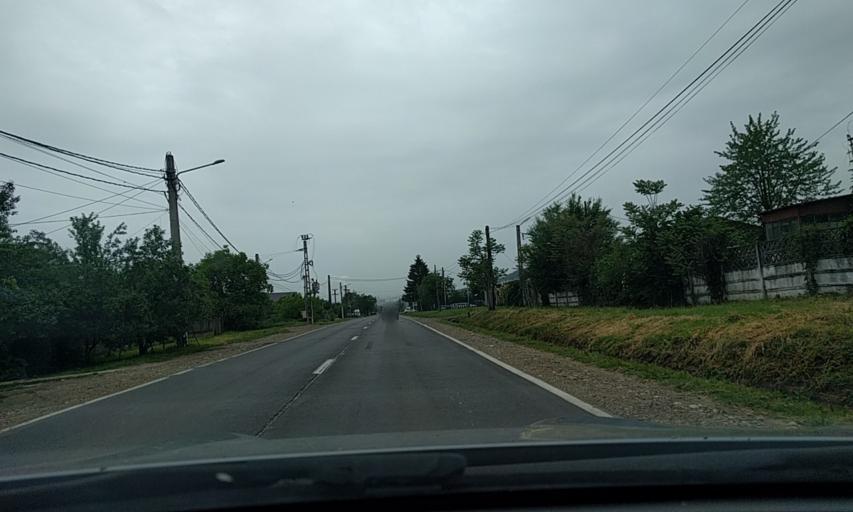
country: RO
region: Dambovita
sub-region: Comuna Aninoasa
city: Aninoasa
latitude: 44.9671
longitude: 25.4354
